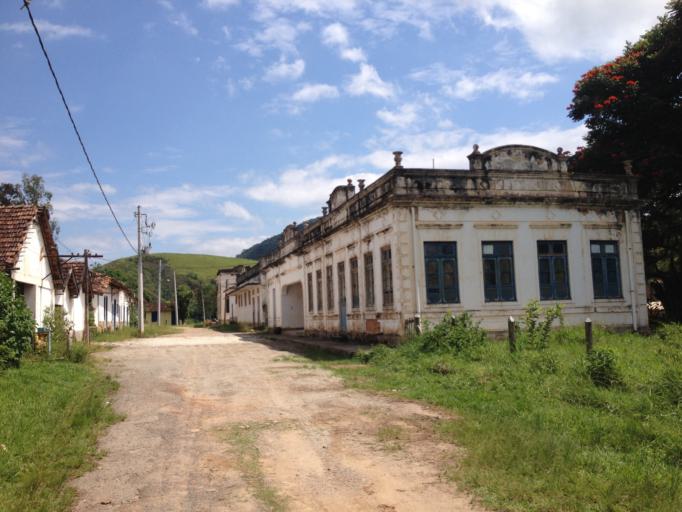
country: BR
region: Rio de Janeiro
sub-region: Valenca
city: Valenca
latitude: -22.1427
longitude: -43.9565
